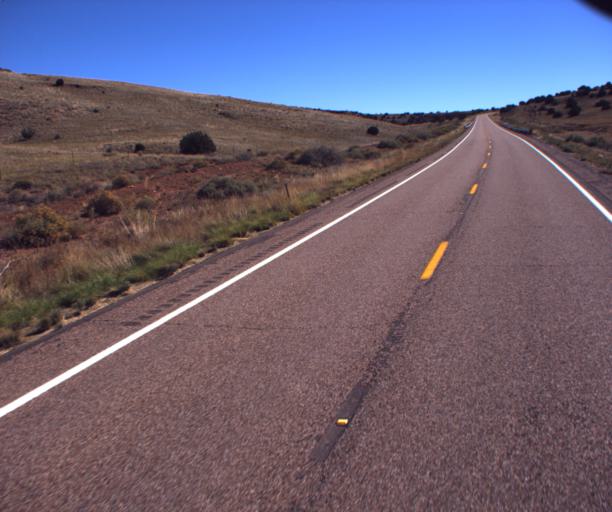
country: US
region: Arizona
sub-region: Apache County
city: Saint Johns
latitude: 34.5708
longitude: -109.5214
